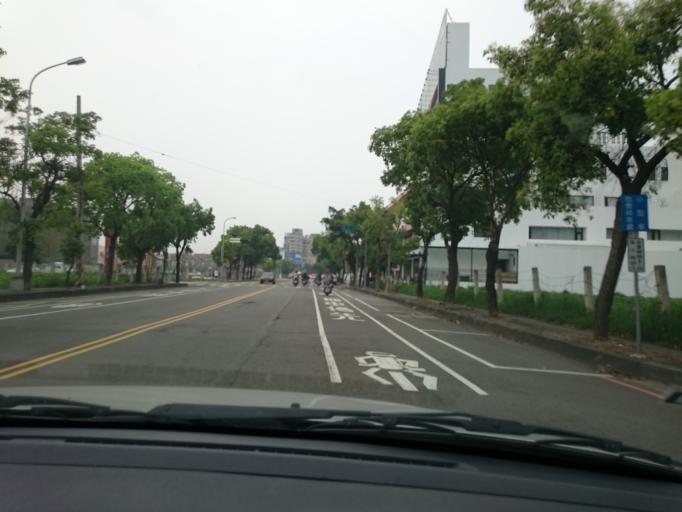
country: TW
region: Taiwan
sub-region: Taichung City
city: Taichung
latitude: 24.1585
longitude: 120.6341
